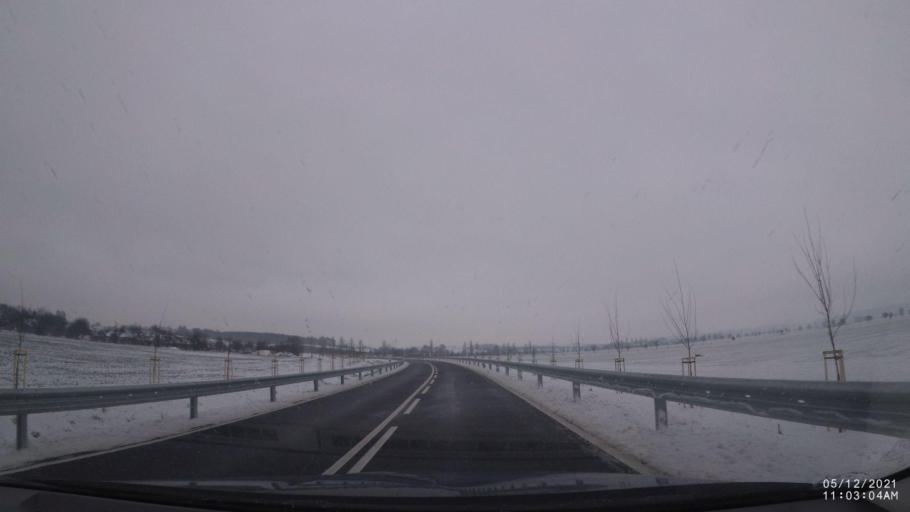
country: CZ
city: Solnice
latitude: 50.1815
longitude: 16.2190
